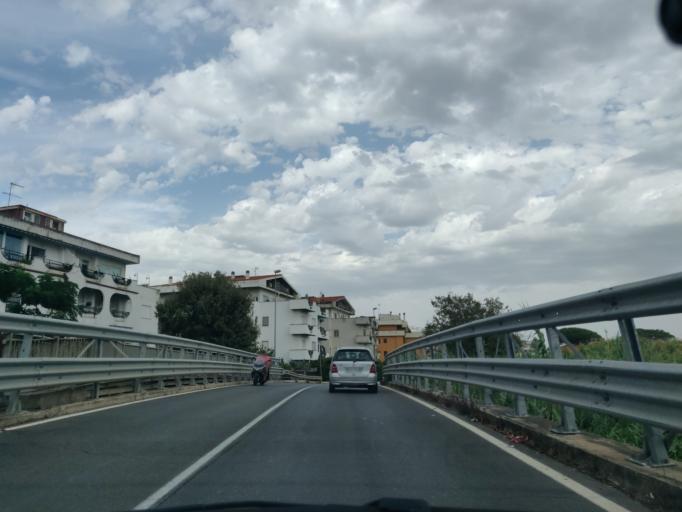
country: IT
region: Latium
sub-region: Citta metropolitana di Roma Capitale
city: Santa Marinella
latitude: 42.0404
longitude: 11.8825
